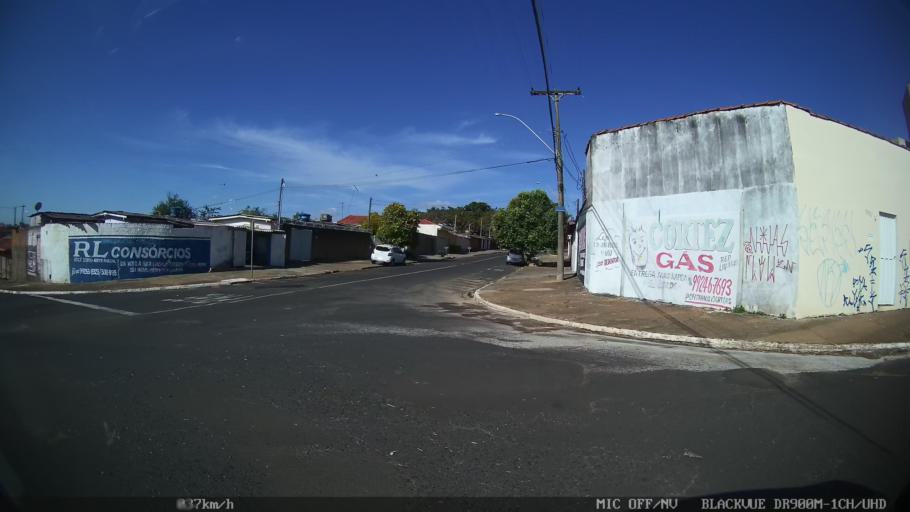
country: BR
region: Sao Paulo
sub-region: Franca
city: Franca
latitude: -20.4976
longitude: -47.4116
